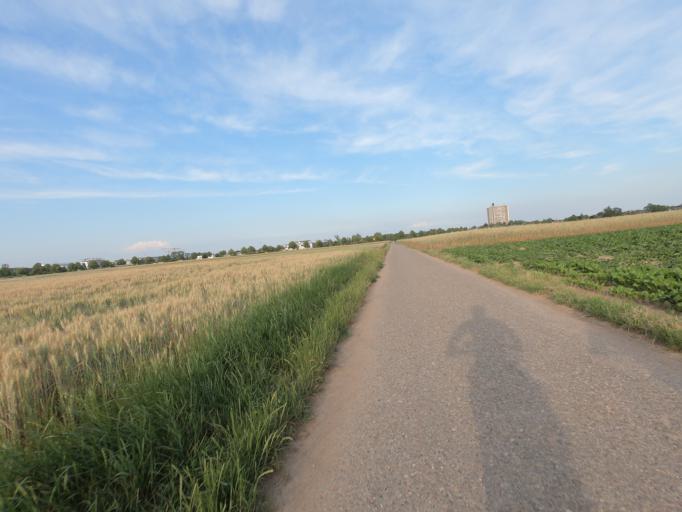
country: DE
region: Hesse
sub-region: Regierungsbezirk Darmstadt
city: Russelsheim
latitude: 49.9693
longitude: 8.4363
